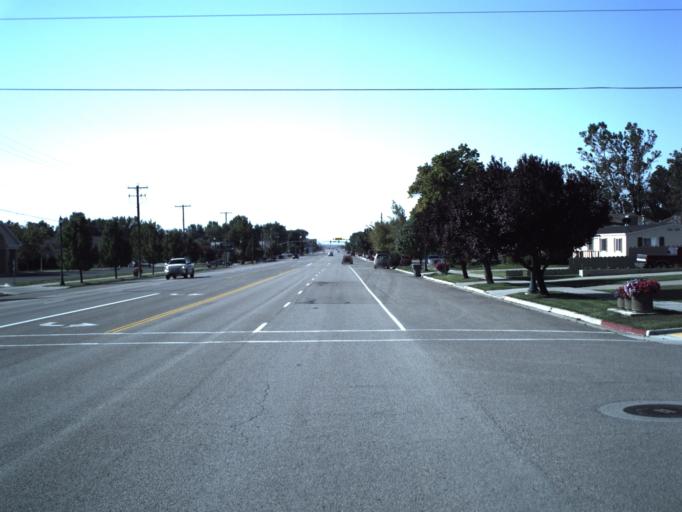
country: US
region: Utah
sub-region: Emery County
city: Huntington
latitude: 39.3318
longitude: -110.9648
